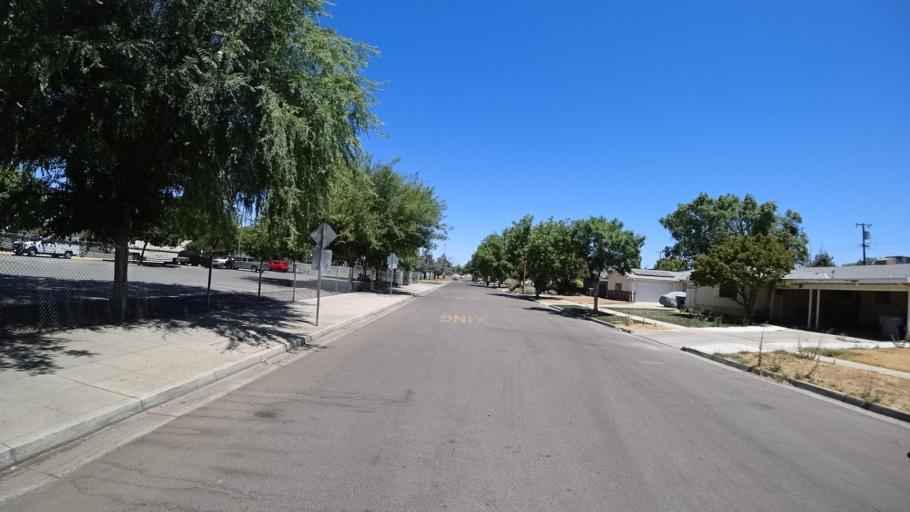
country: US
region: California
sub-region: Fresno County
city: Fresno
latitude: 36.8026
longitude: -119.7792
